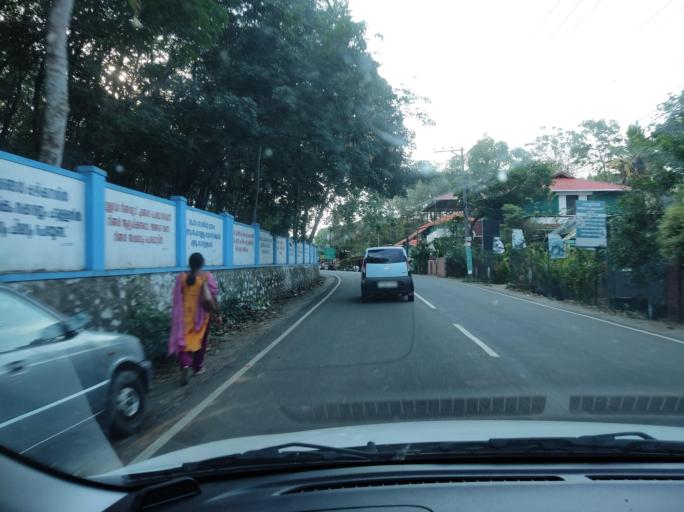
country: IN
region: Kerala
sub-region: Kottayam
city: Kottayam
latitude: 9.6481
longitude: 76.5223
